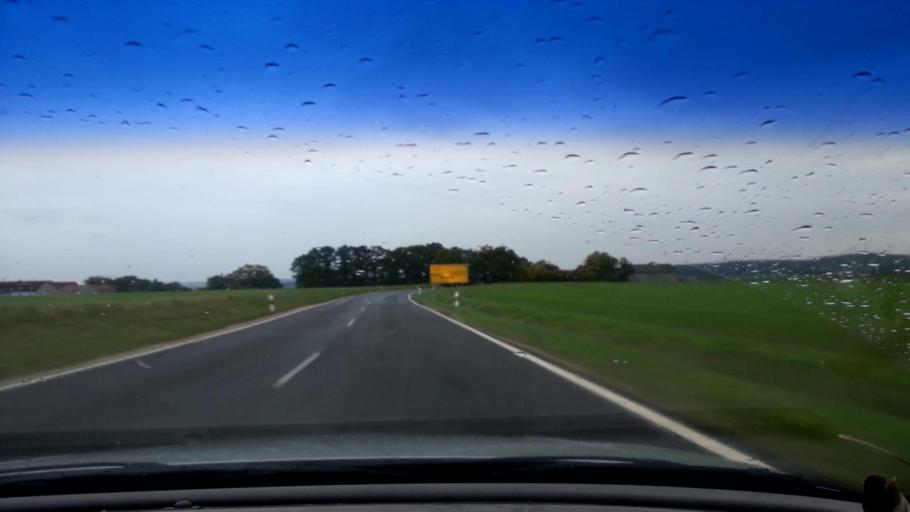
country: DE
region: Bavaria
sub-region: Upper Franconia
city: Priesendorf
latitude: 49.8629
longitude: 10.7180
